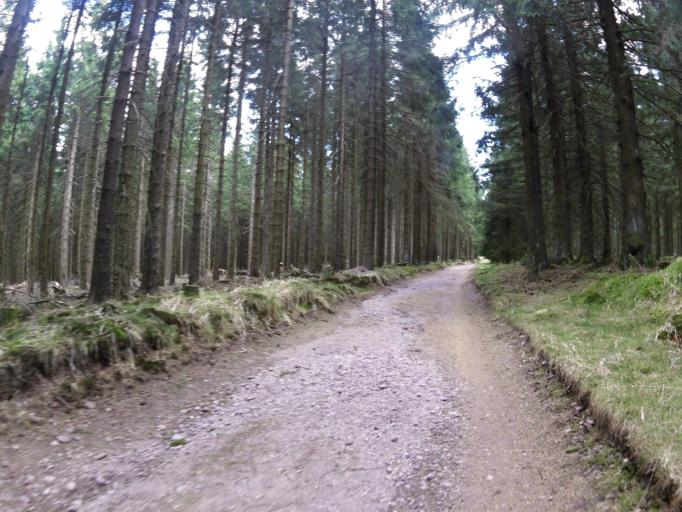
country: DE
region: Thuringia
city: Unterschonau
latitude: 50.7528
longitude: 10.5682
